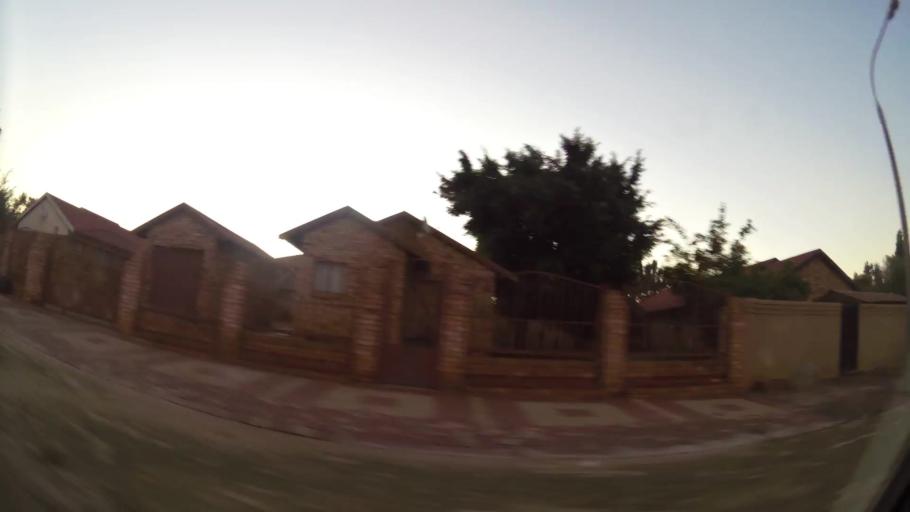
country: ZA
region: North-West
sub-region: Bojanala Platinum District Municipality
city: Rustenburg
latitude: -25.6609
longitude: 27.2108
